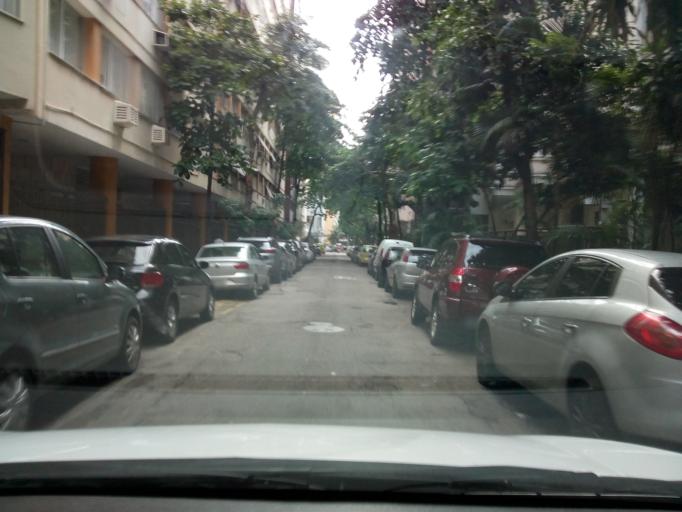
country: BR
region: Rio de Janeiro
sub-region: Rio De Janeiro
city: Rio de Janeiro
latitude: -22.9734
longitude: -43.1874
